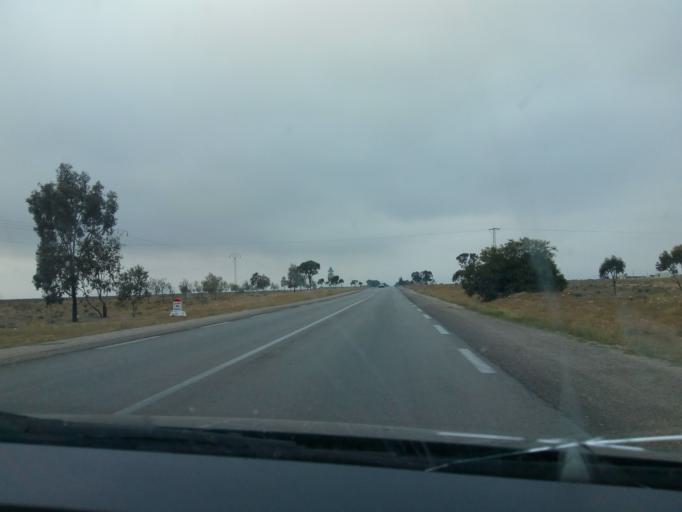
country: TN
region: Madanin
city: Medenine
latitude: 33.2663
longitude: 10.4661
